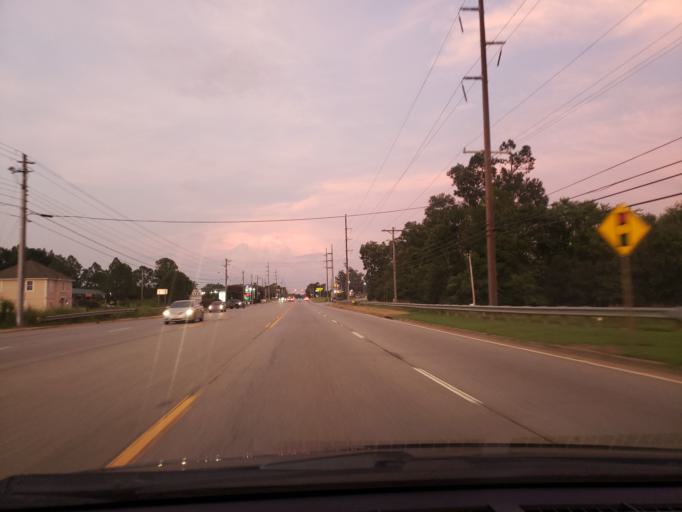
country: US
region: Georgia
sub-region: Dougherty County
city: Albany
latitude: 31.5856
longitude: -84.2227
